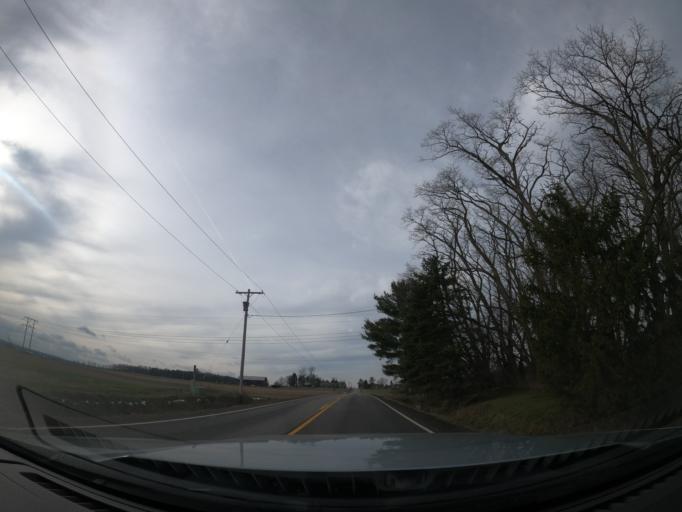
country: US
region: New York
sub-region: Yates County
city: Dundee
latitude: 42.5000
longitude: -76.9375
